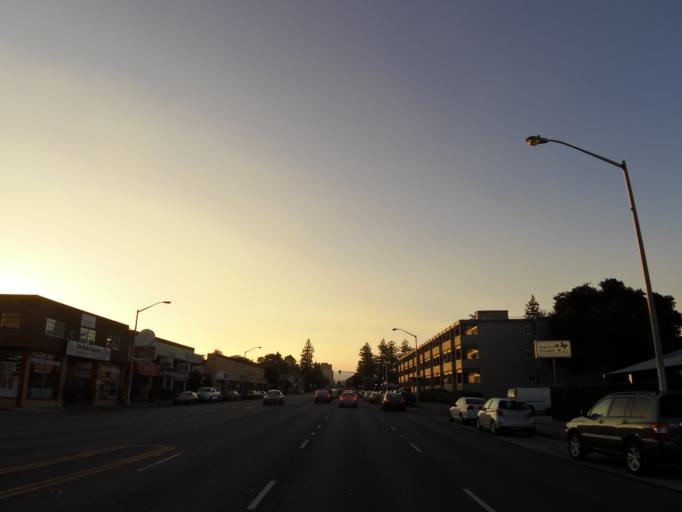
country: US
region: California
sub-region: San Mateo County
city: San Mateo
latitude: 37.5551
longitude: -122.3172
